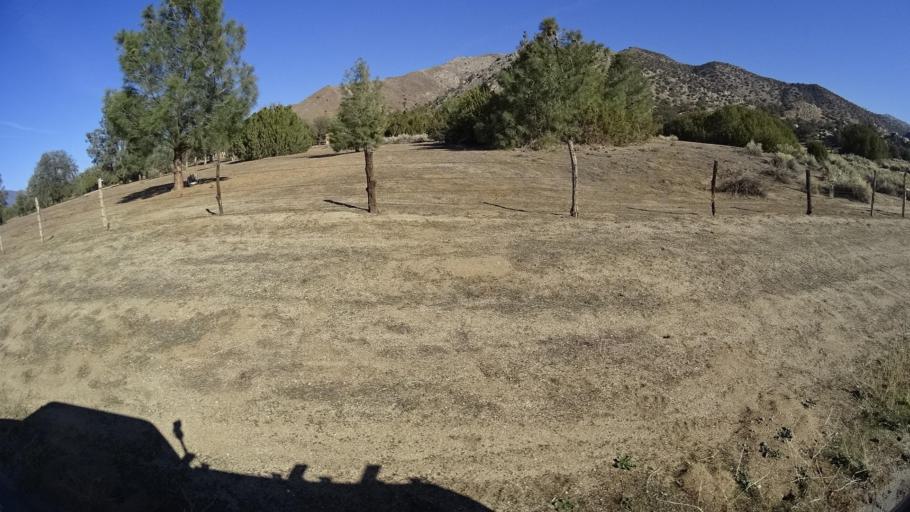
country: US
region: California
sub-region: Kern County
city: Bodfish
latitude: 35.4021
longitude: -118.4775
